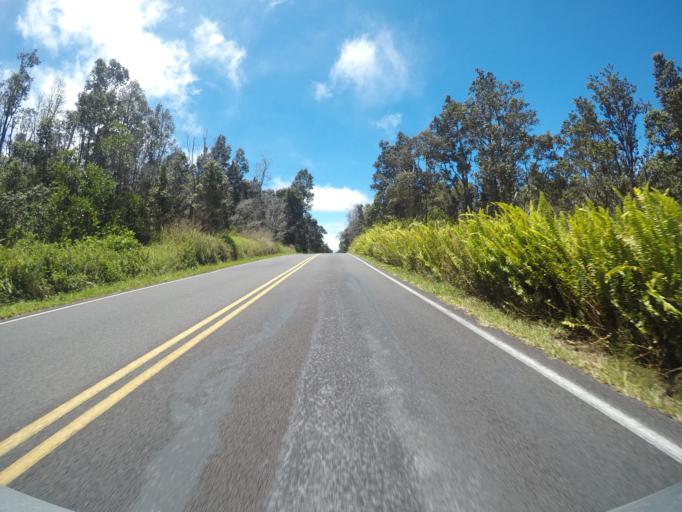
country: US
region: Hawaii
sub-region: Hawaii County
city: Volcano
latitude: 19.3933
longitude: -155.2505
